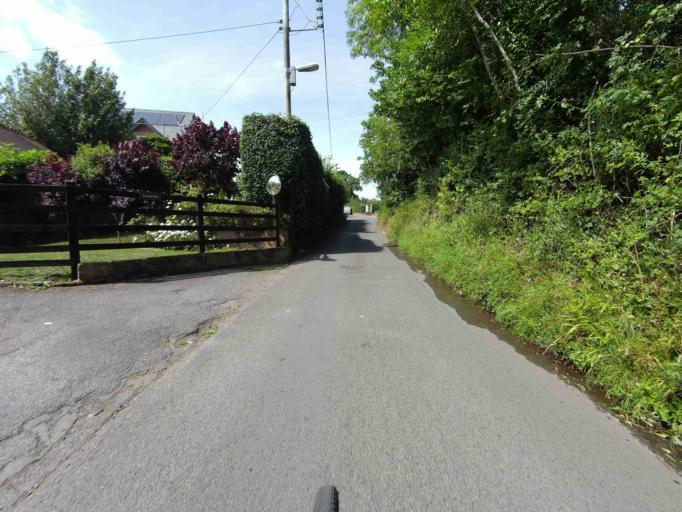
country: GB
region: England
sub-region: Devon
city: Topsham
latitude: 50.6695
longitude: -3.4413
